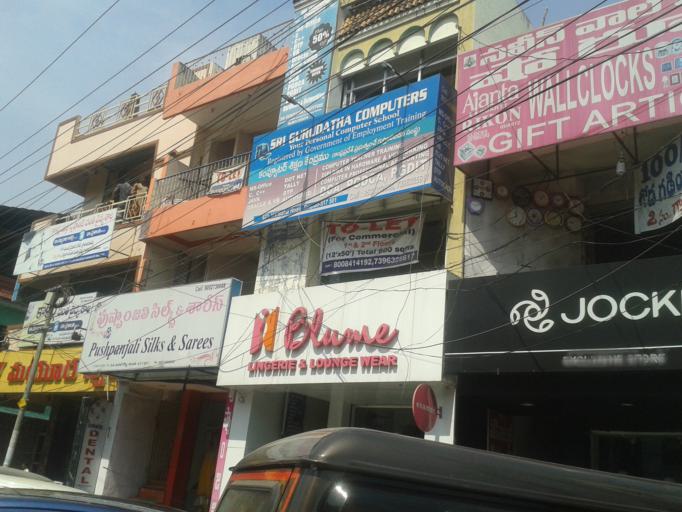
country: IN
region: Andhra Pradesh
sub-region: Chittoor
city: Tirupati
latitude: 13.6371
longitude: 79.4218
